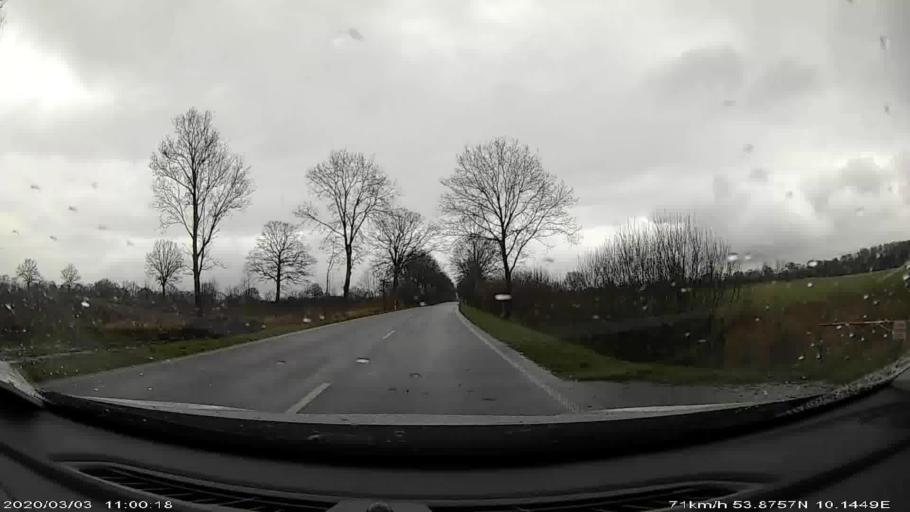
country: DE
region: Schleswig-Holstein
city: Stuvenborn
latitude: 53.8776
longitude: 10.1500
